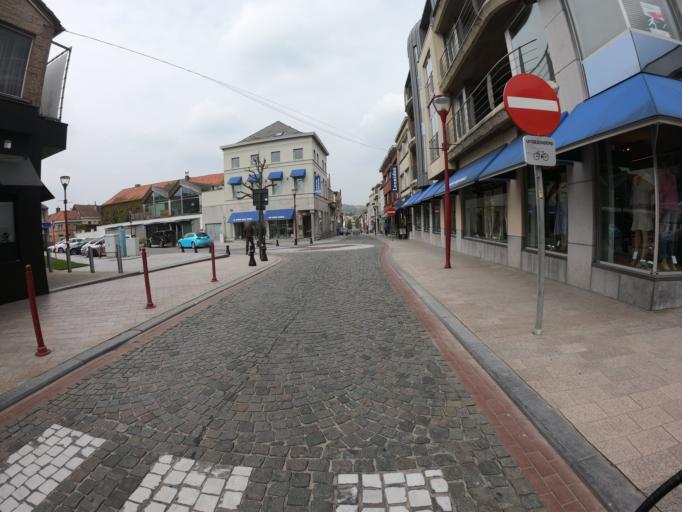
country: BE
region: Flanders
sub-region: Provincie Oost-Vlaanderen
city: Ronse
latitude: 50.7473
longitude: 3.5990
